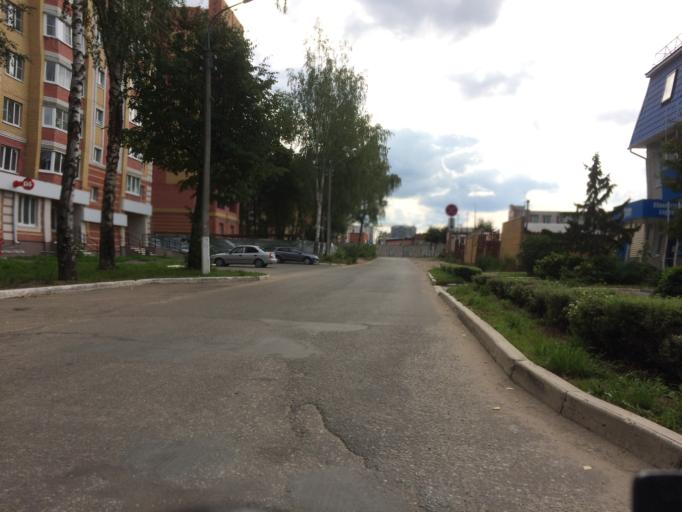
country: RU
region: Mariy-El
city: Yoshkar-Ola
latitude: 56.6341
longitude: 47.8751
